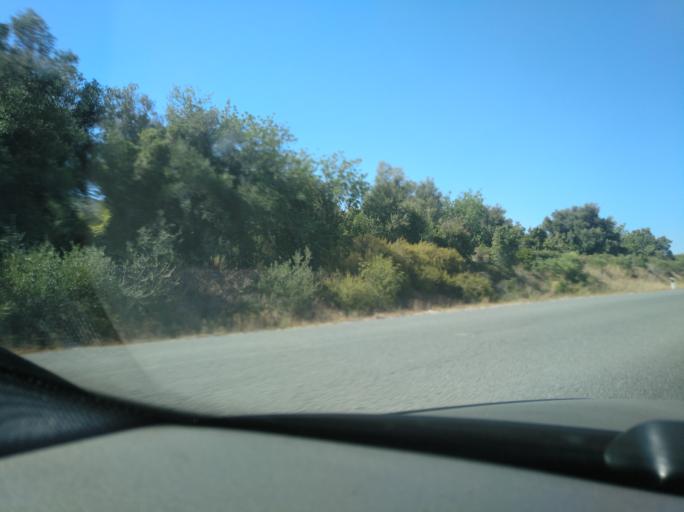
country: PT
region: Faro
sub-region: Olhao
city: Moncarapacho
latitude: 37.0976
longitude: -7.8006
